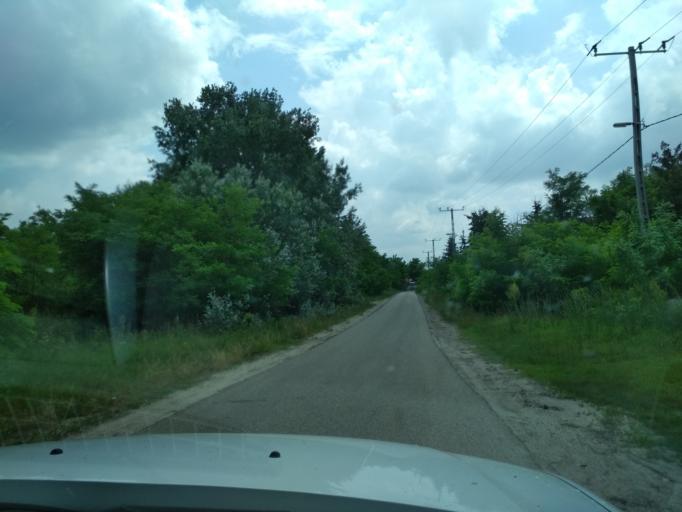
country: HU
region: Pest
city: Tapioszentmarton
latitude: 47.3748
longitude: 19.7561
